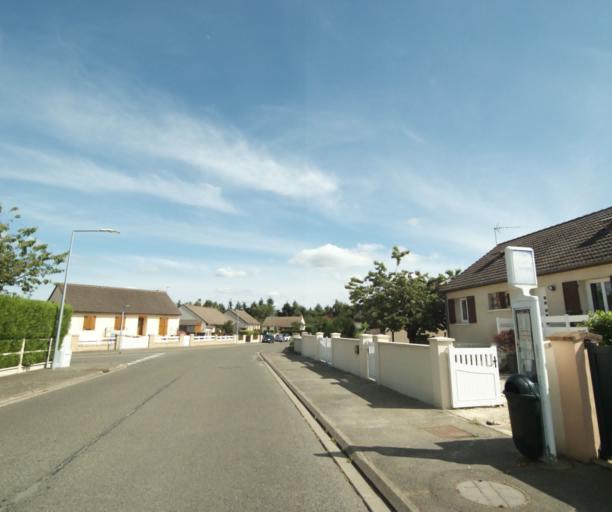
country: FR
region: Centre
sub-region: Departement d'Eure-et-Loir
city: Luce
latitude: 48.4301
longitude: 1.4422
